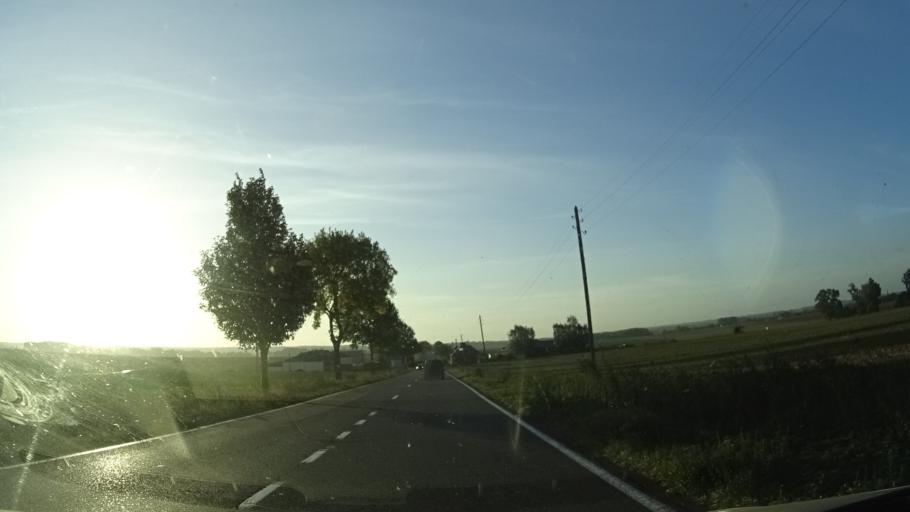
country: FR
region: Nord-Pas-de-Calais
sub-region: Departement du Nord
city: Marpent
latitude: 50.3505
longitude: 4.0680
